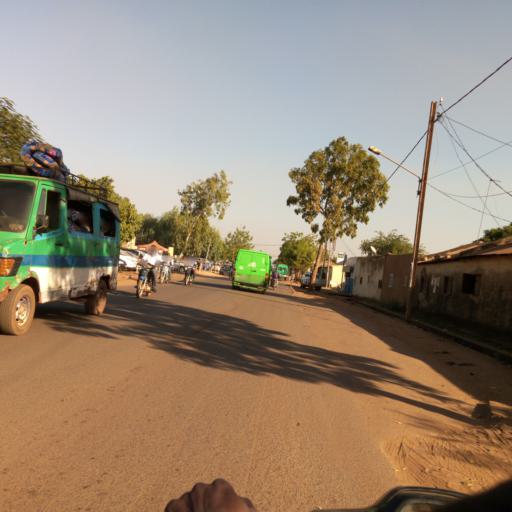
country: ML
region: Bamako
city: Bamako
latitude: 12.6536
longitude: -8.0199
